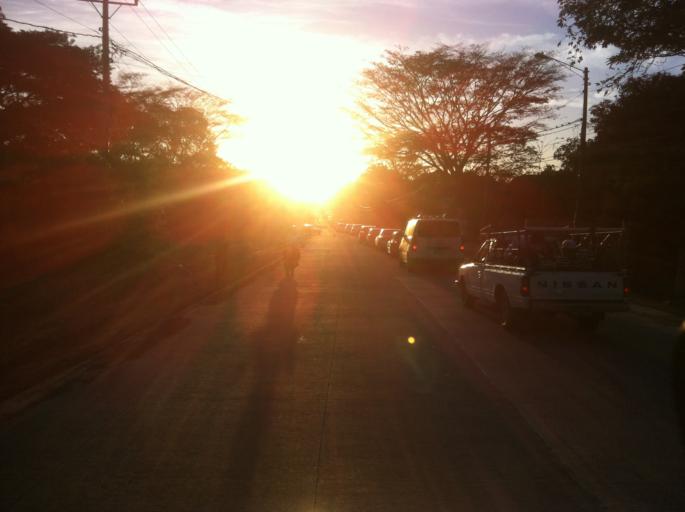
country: NI
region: Managua
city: Ciudad Sandino
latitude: 12.1063
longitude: -86.3275
